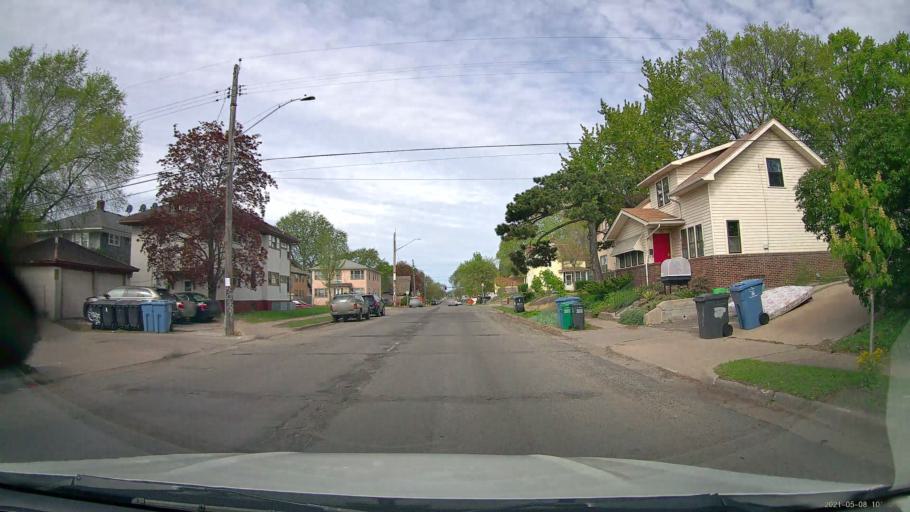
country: US
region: Minnesota
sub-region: Hennepin County
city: Minneapolis
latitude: 44.9396
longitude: -93.2656
